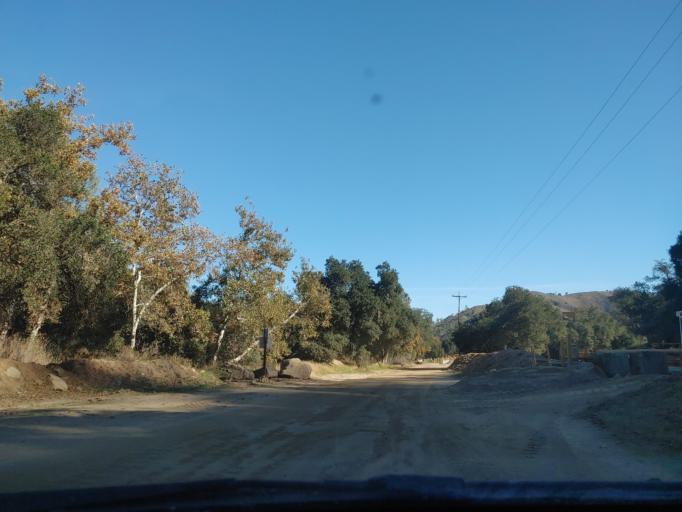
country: US
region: California
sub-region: San Benito County
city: Ridgemark
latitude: 36.6875
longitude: -121.3499
